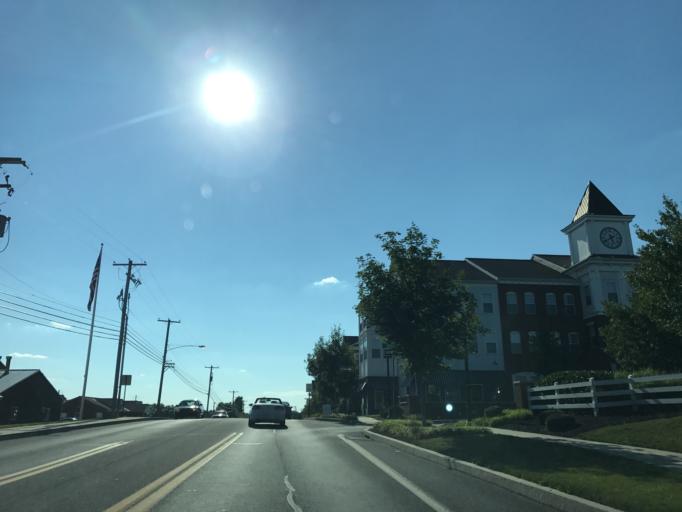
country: US
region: Pennsylvania
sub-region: Lancaster County
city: Mount Joy
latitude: 40.1160
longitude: -76.5271
